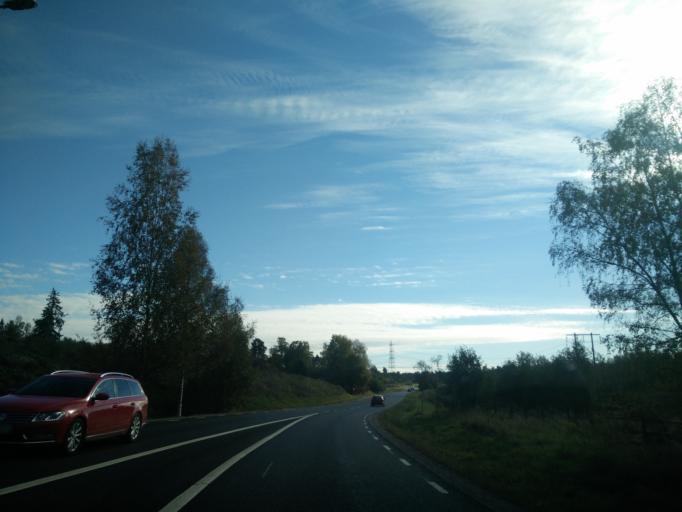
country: SE
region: Stockholm
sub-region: Upplands Vasby Kommun
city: Upplands Vaesby
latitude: 59.5098
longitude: 17.9632
